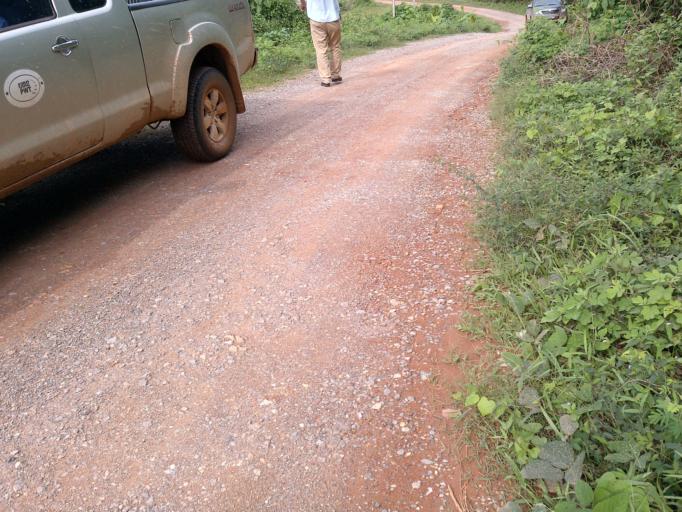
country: LA
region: Xiagnabouli
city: Muang Kenthao
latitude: 17.9145
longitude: 101.3605
